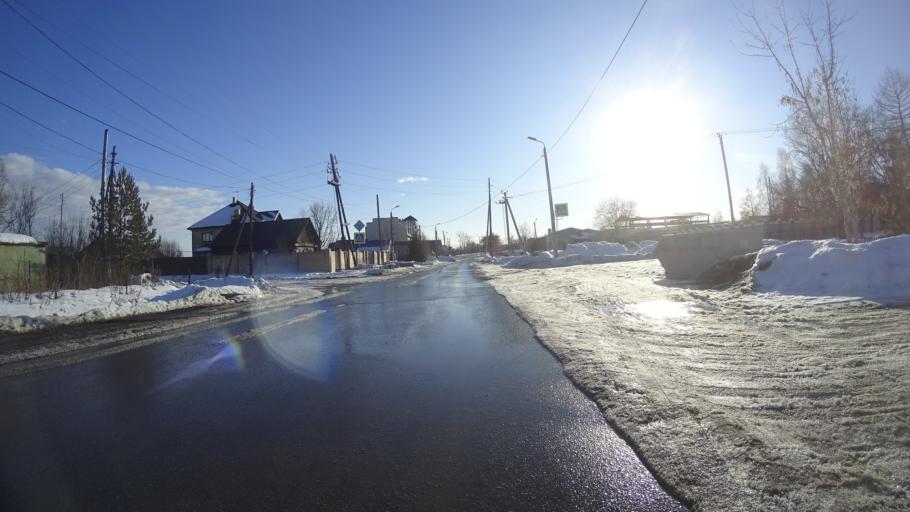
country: RU
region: Chelyabinsk
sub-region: Gorod Chelyabinsk
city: Chelyabinsk
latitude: 55.1511
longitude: 61.3086
